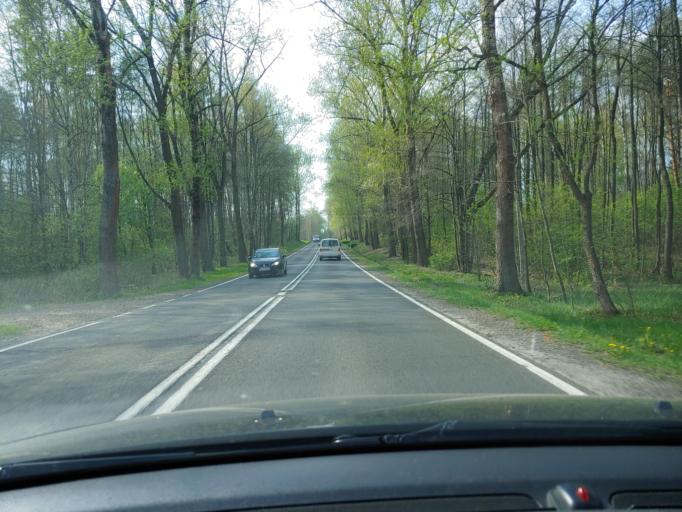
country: PL
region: Lesser Poland Voivodeship
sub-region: Powiat krakowski
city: Filipowice
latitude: 50.1400
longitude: 19.5546
